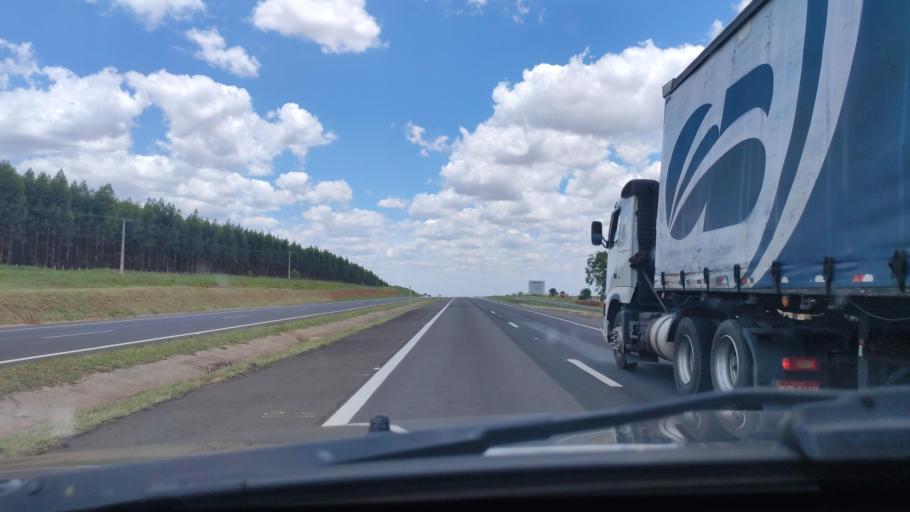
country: BR
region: Sao Paulo
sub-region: Duartina
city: Duartina
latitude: -22.6039
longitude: -49.3828
